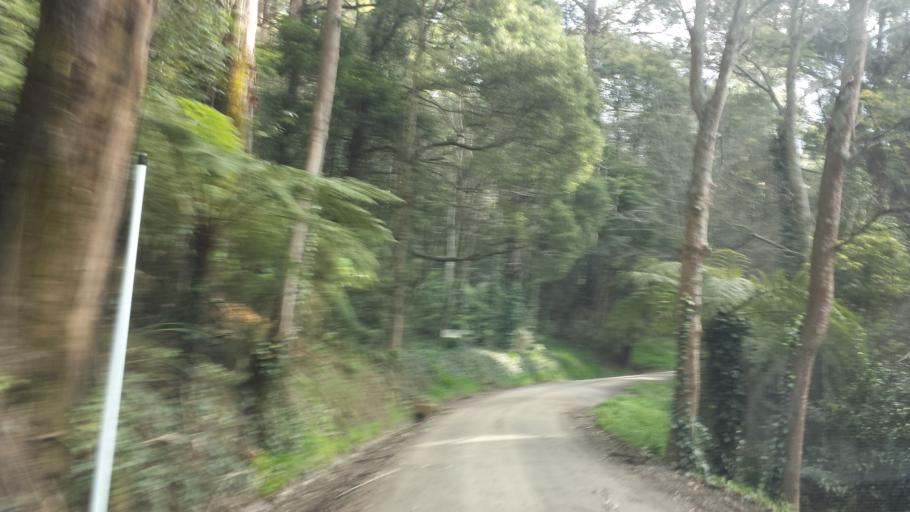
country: AU
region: Victoria
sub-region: Yarra Ranges
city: Kallista
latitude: -37.8856
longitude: 145.3817
